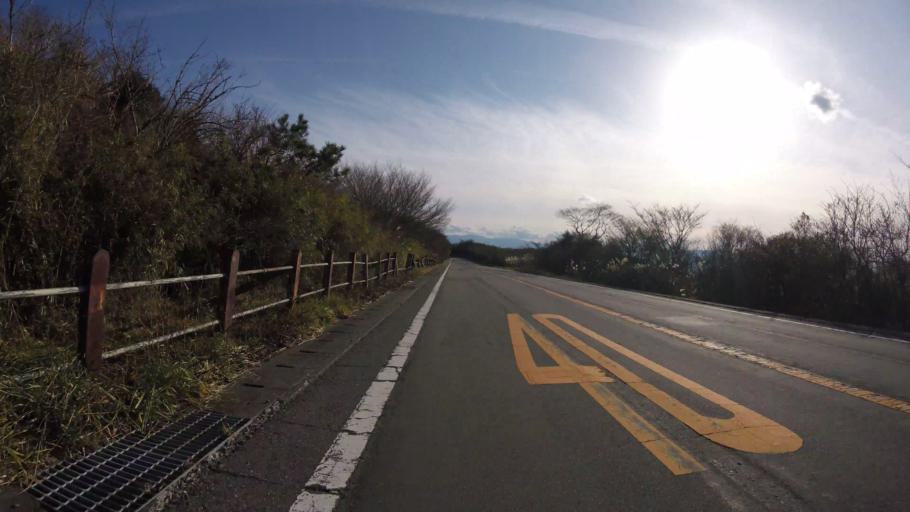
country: JP
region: Kanagawa
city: Hakone
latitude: 35.1525
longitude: 139.0253
